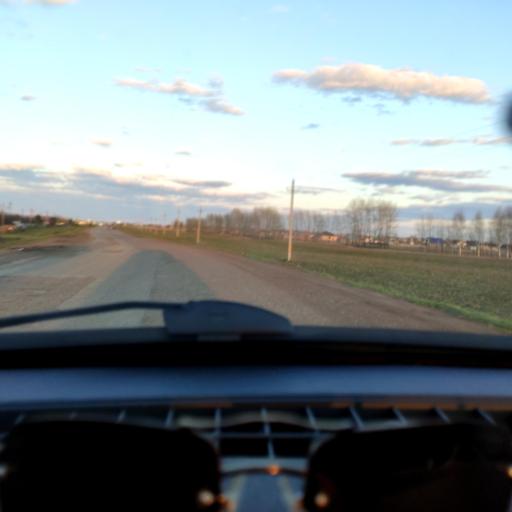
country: RU
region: Bashkortostan
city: Kabakovo
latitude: 54.5427
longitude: 56.1224
